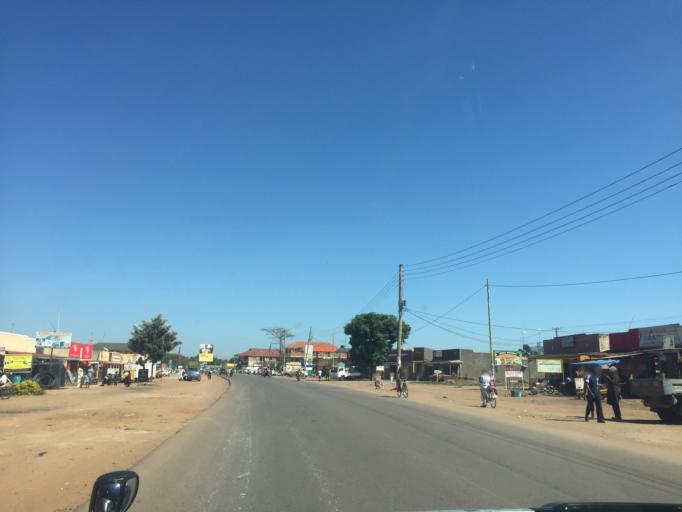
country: UG
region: Central Region
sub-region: Luwero District
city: Luwero
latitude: 0.8295
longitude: 32.5014
